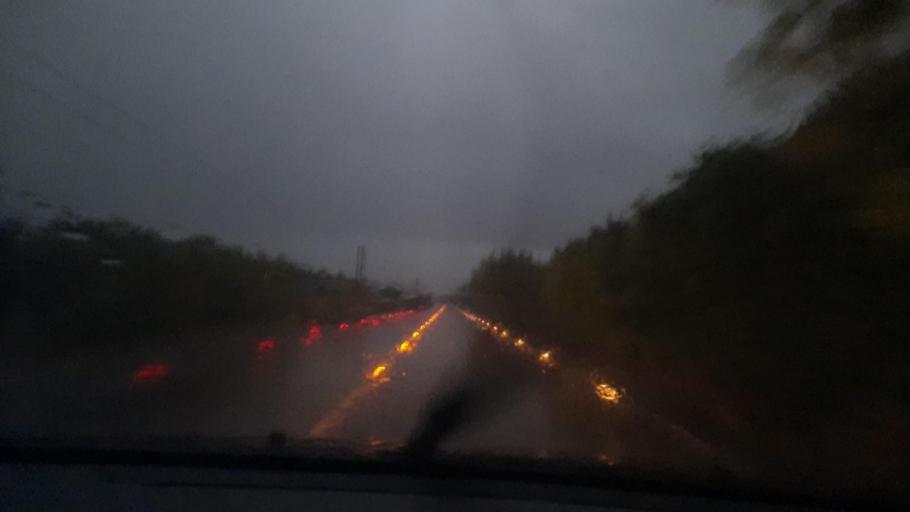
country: HN
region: Cortes
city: Potrerillos
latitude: 15.6407
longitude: -88.4206
